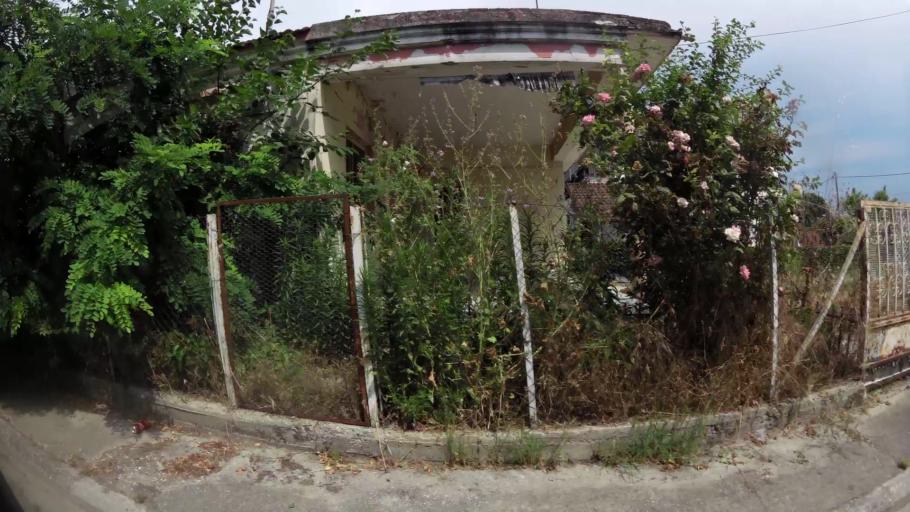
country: GR
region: Central Macedonia
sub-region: Nomos Pierias
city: Korinos
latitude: 40.3154
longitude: 22.5780
